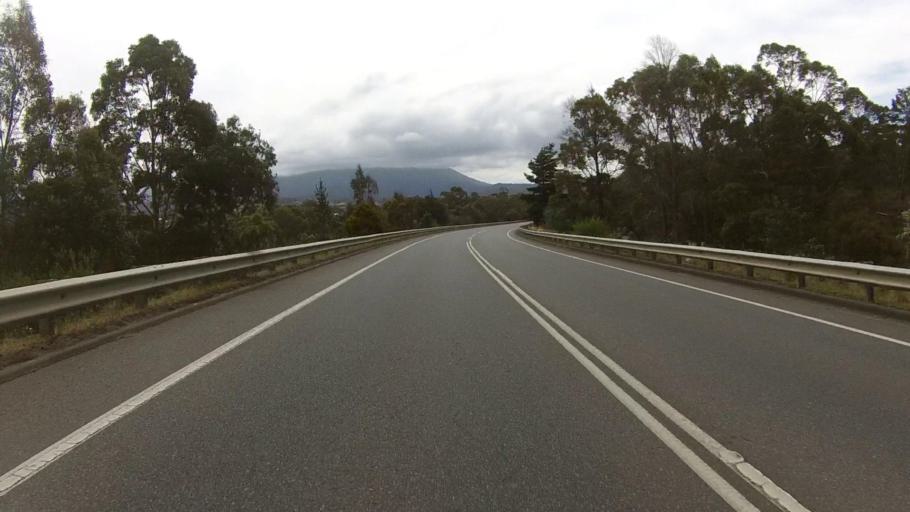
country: AU
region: Tasmania
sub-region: Kingborough
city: Kingston
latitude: -42.9945
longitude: 147.2951
